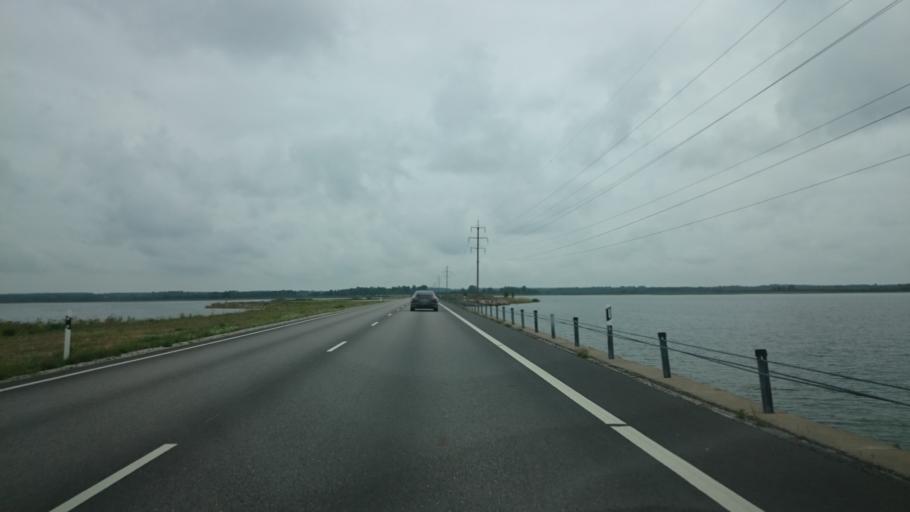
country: EE
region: Saare
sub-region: Orissaare vald
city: Orissaare
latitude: 58.5616
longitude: 23.1550
